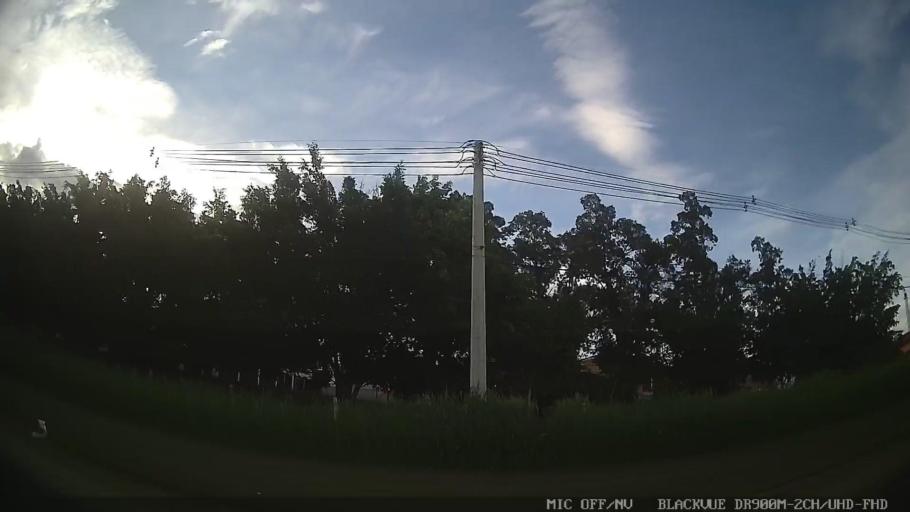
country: BR
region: Sao Paulo
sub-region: Tiete
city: Tiete
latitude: -23.0653
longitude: -47.7291
